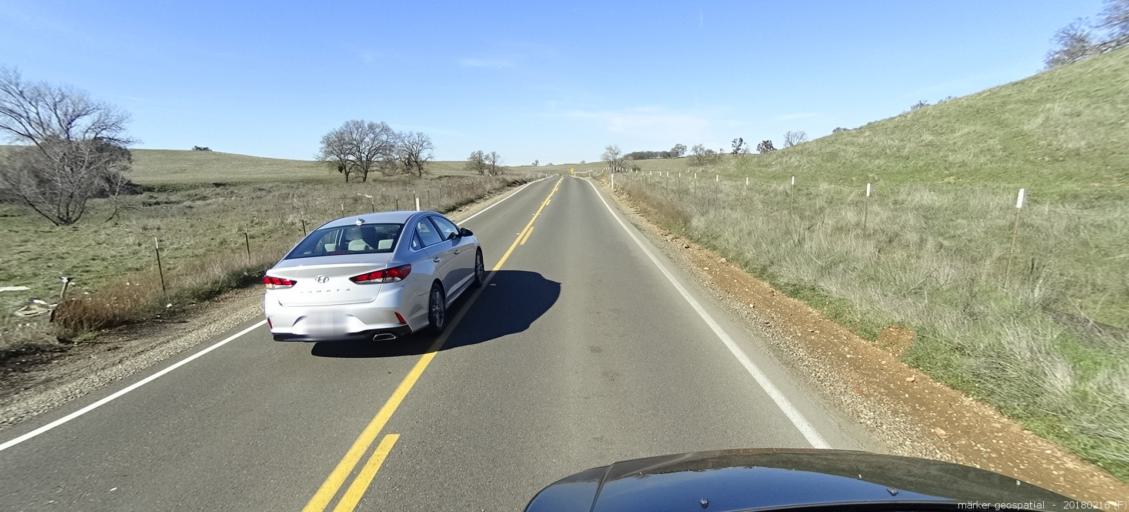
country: US
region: California
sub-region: Sacramento County
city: Rancho Murieta
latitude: 38.5520
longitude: -121.1146
